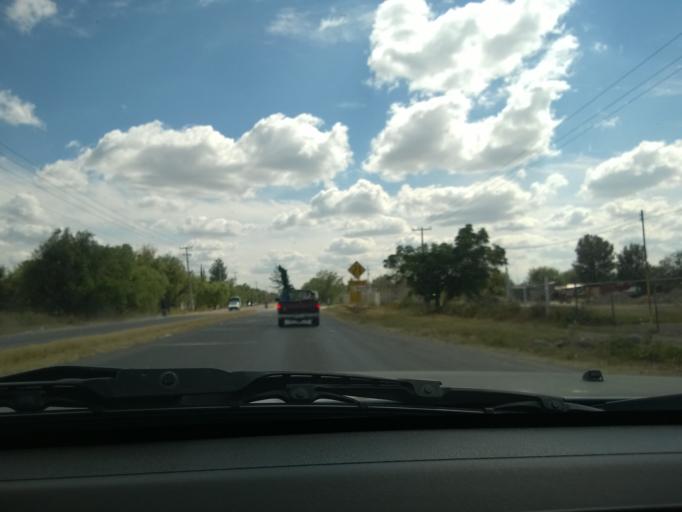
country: MX
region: Guanajuato
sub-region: Leon
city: El CERESO
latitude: 20.9926
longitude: -101.7028
